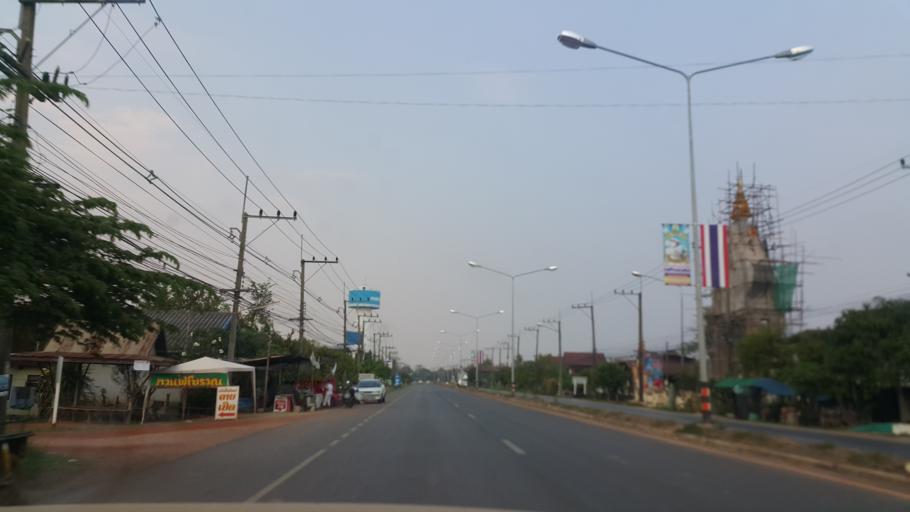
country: TH
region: Nakhon Phanom
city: That Phanom
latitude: 16.9794
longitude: 104.7279
